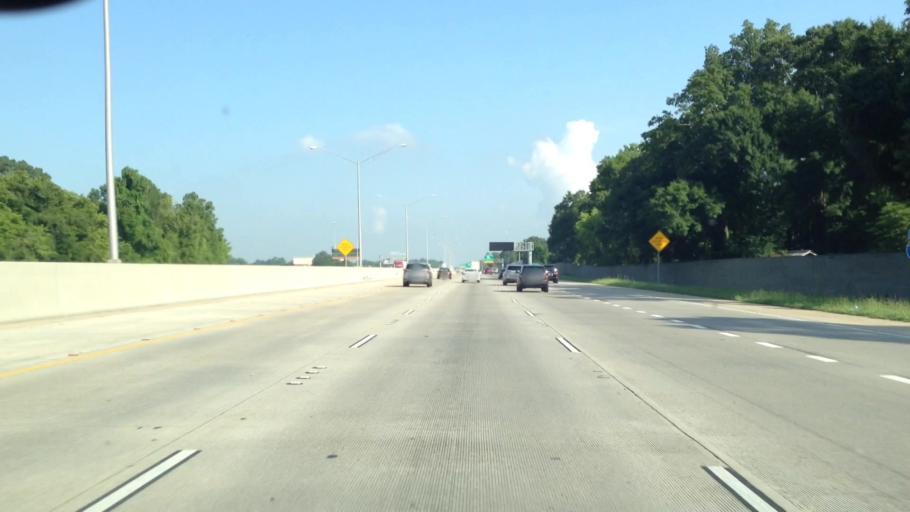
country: US
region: Louisiana
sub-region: East Baton Rouge Parish
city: Inniswold
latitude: 30.3989
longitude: -91.0904
